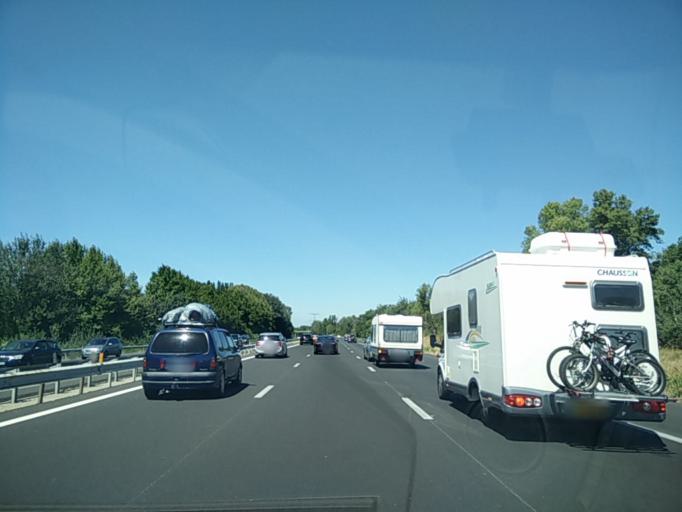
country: FR
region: Provence-Alpes-Cote d'Azur
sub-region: Departement des Bouches-du-Rhone
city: Cabannes
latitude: 43.8600
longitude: 4.9761
